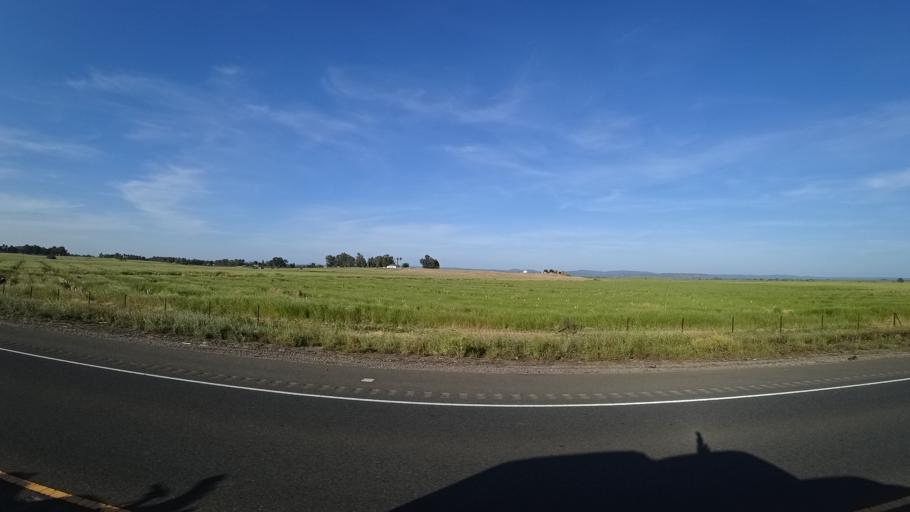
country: US
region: California
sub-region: Placer County
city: Sheridan
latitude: 38.9690
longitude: -121.3665
